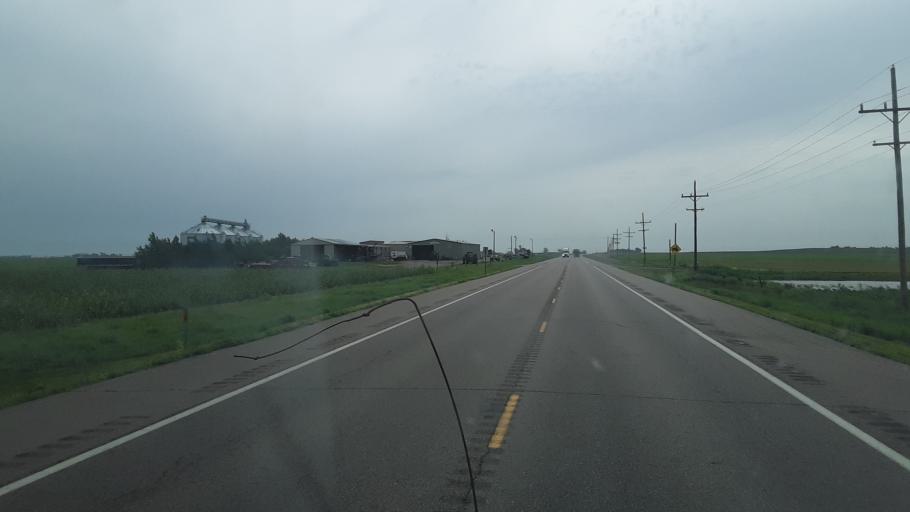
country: US
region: Kansas
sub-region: Edwards County
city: Kinsley
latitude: 37.9275
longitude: -99.2974
